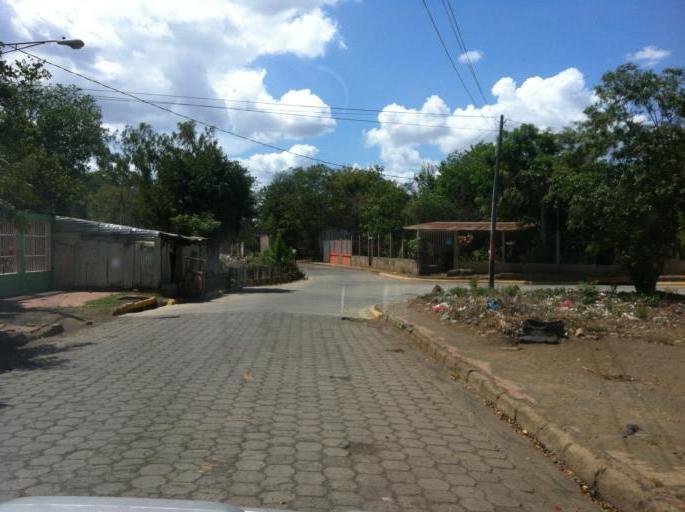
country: NI
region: Masaya
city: Masaya
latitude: 11.9684
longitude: -86.0966
